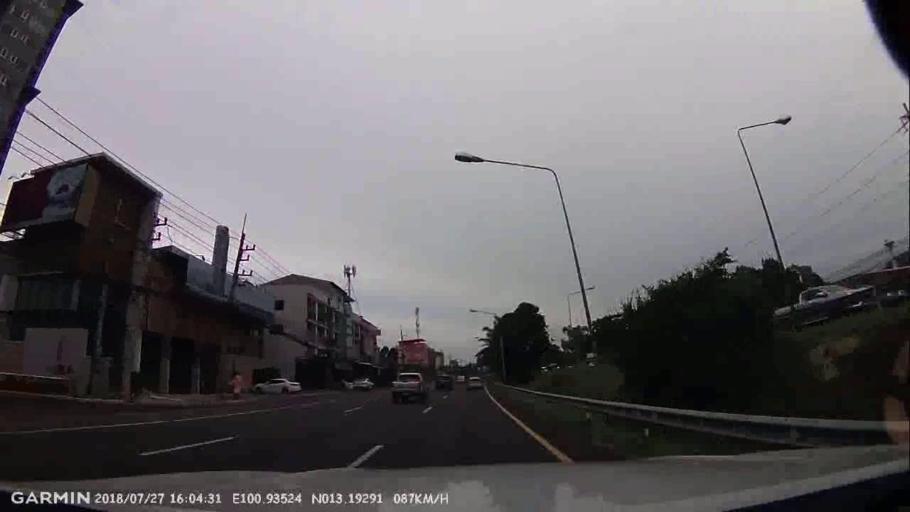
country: TH
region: Chon Buri
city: Si Racha
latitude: 13.1929
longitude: 100.9352
